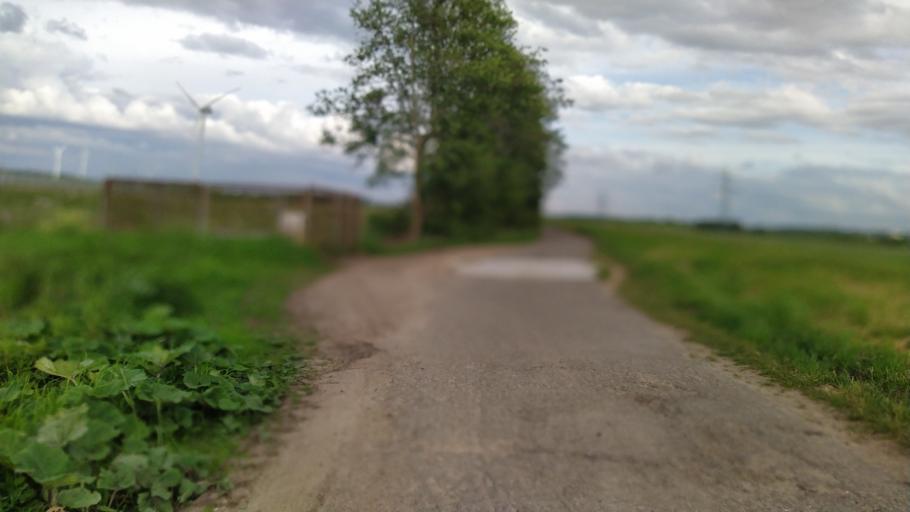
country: DE
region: Lower Saxony
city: Neu Wulmstorf
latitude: 53.4950
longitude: 9.8435
